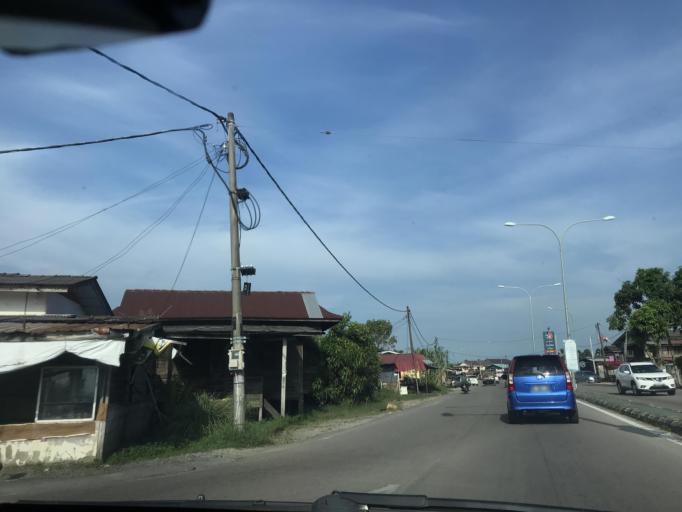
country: MY
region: Kelantan
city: Kota Bharu
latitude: 6.1202
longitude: 102.2865
